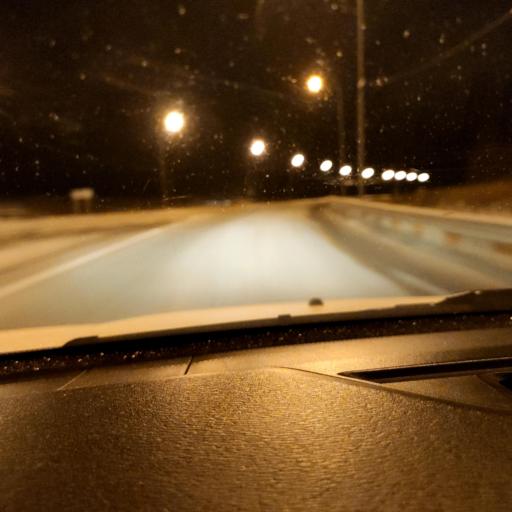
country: RU
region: Samara
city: Smyshlyayevka
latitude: 53.1459
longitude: 50.3911
